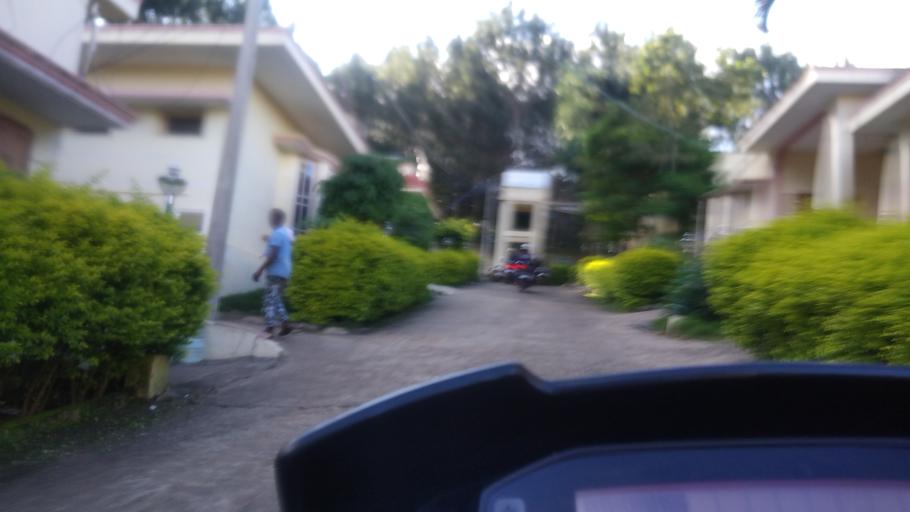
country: IN
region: Tamil Nadu
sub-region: Salem
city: Salem
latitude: 11.7710
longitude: 78.2121
